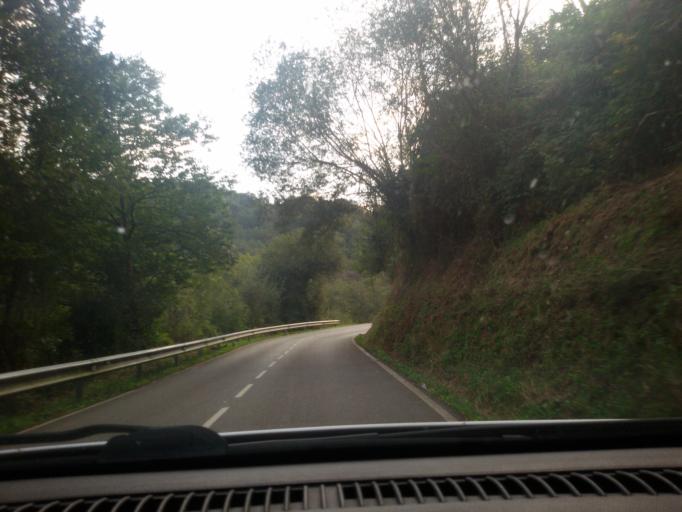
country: ES
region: Asturias
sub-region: Province of Asturias
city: Bimenes
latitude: 43.3363
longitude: -5.5792
